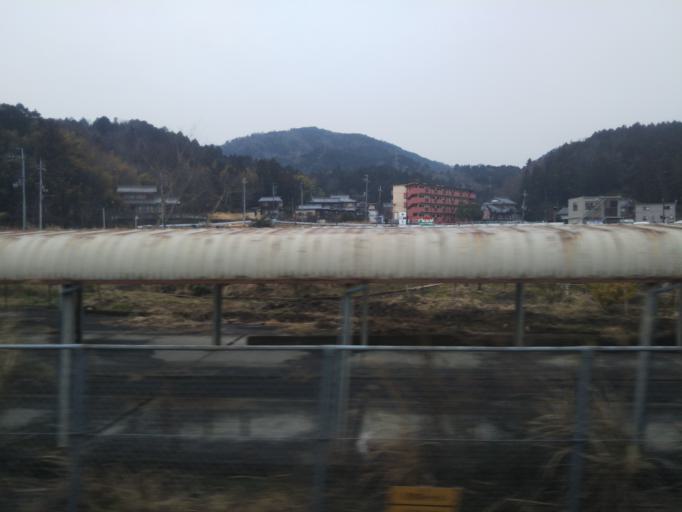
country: JP
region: Shiga Prefecture
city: Minakuchicho-matoba
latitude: 34.9843
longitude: 136.1130
